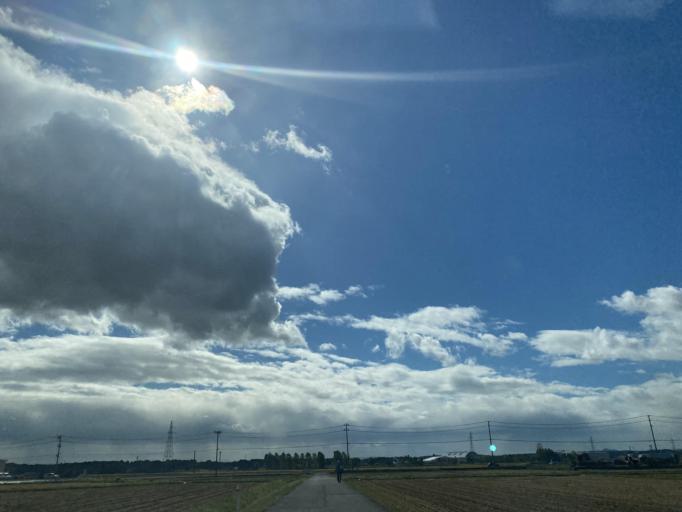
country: JP
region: Fukushima
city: Koriyama
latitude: 37.3758
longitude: 140.3320
